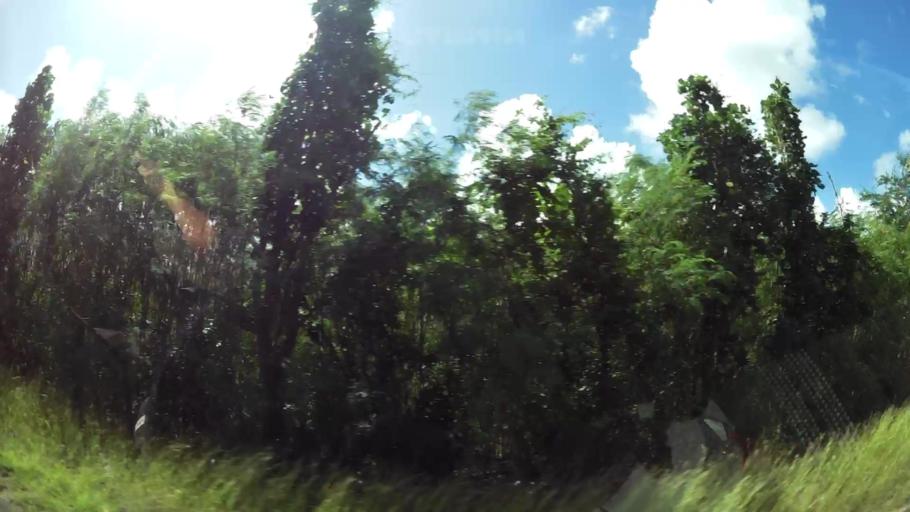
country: GP
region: Guadeloupe
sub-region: Guadeloupe
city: Anse-Bertrand
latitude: 16.4620
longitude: -61.4855
